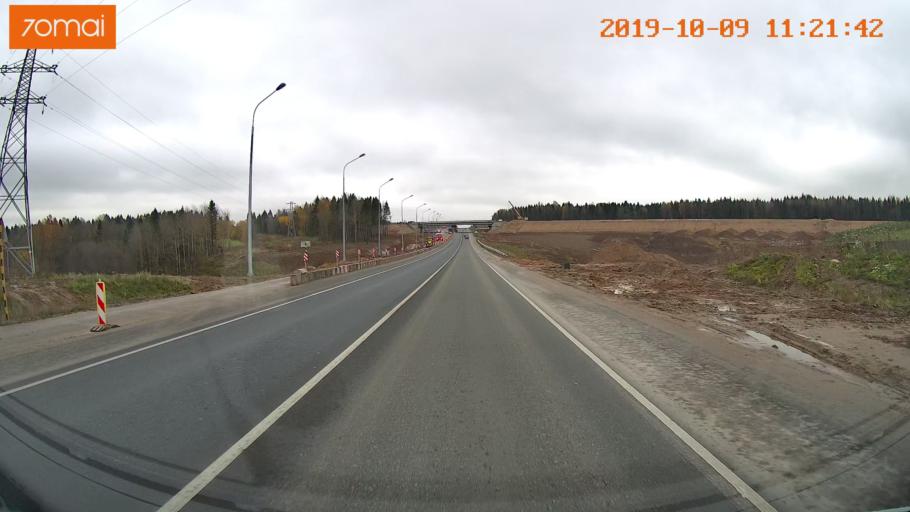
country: RU
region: Vologda
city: Vologda
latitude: 59.1375
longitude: 39.9517
